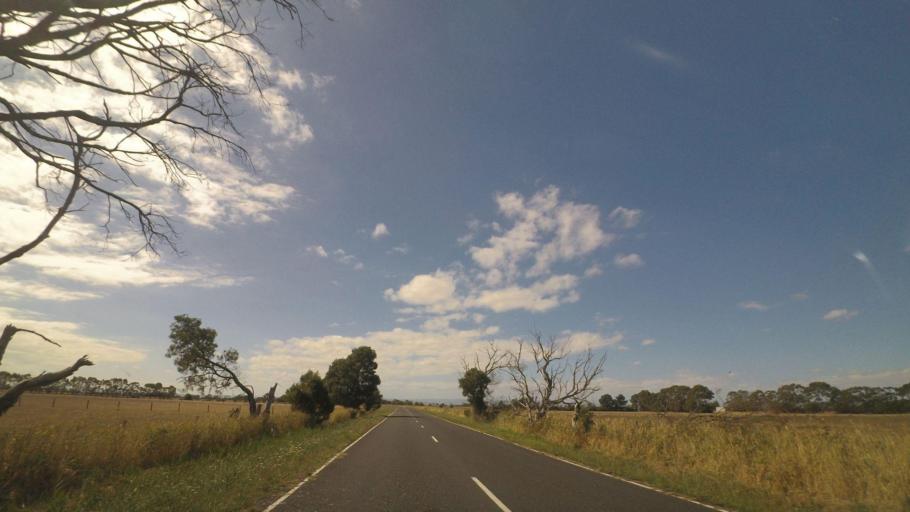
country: AU
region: Victoria
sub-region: Cardinia
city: Garfield
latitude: -38.2380
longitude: 145.6389
